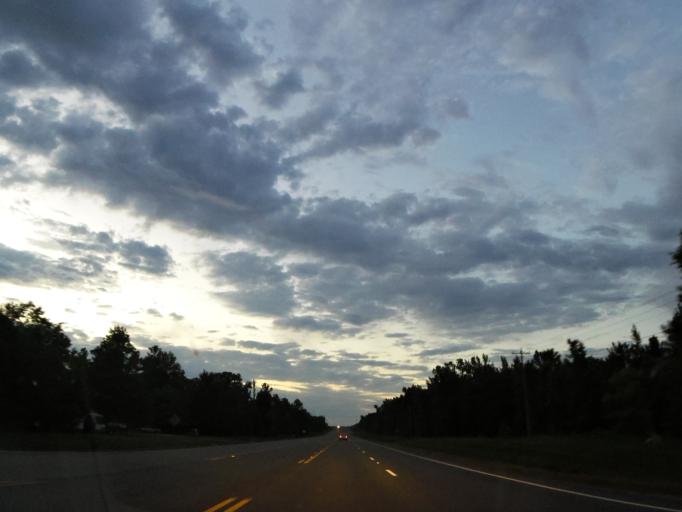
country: US
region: Alabama
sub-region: Marion County
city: Winfield
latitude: 33.9746
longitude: -87.7742
